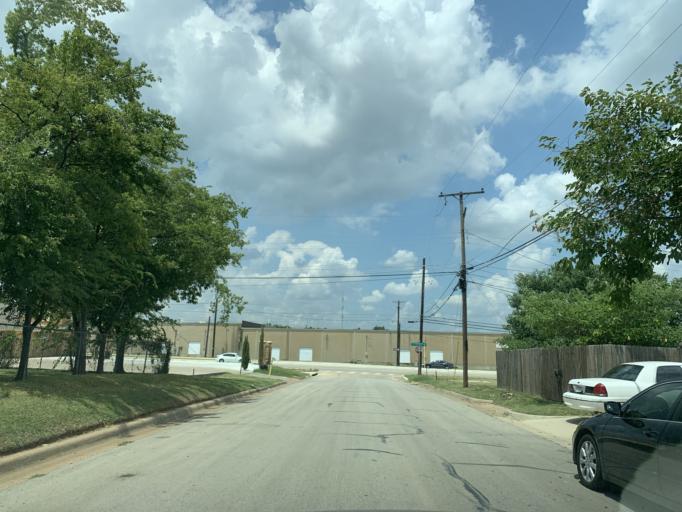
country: US
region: Texas
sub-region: Tarrant County
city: Forest Hill
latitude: 32.7293
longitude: -97.2342
